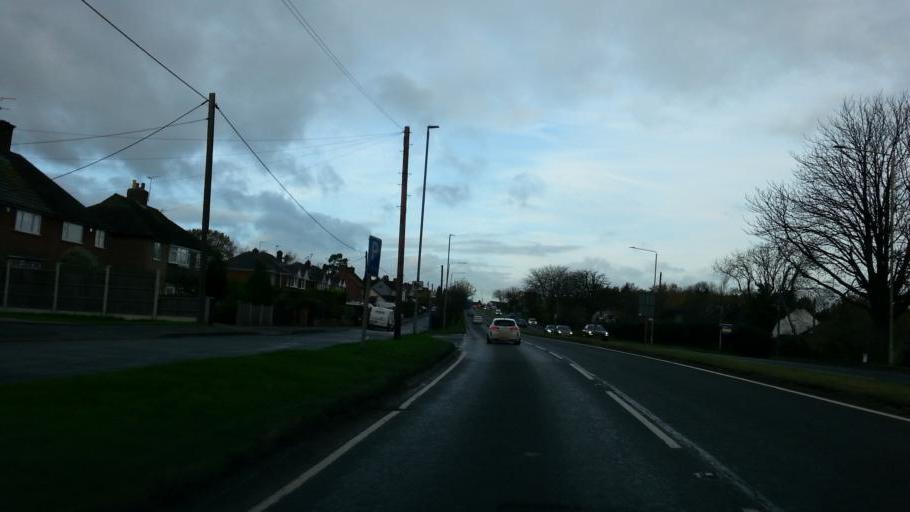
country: GB
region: England
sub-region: Leicestershire
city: Markfield
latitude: 52.6814
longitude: -1.2601
